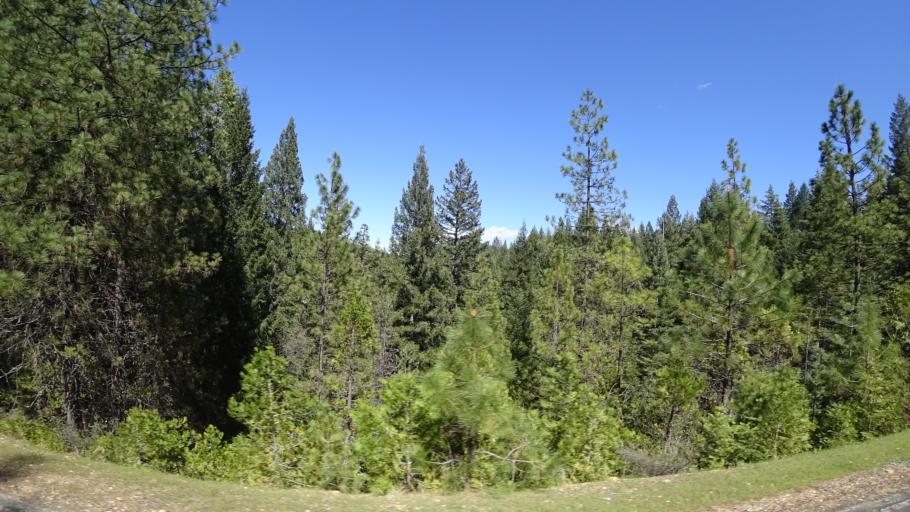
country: US
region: California
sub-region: Trinity County
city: Lewiston
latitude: 40.9025
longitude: -122.7877
